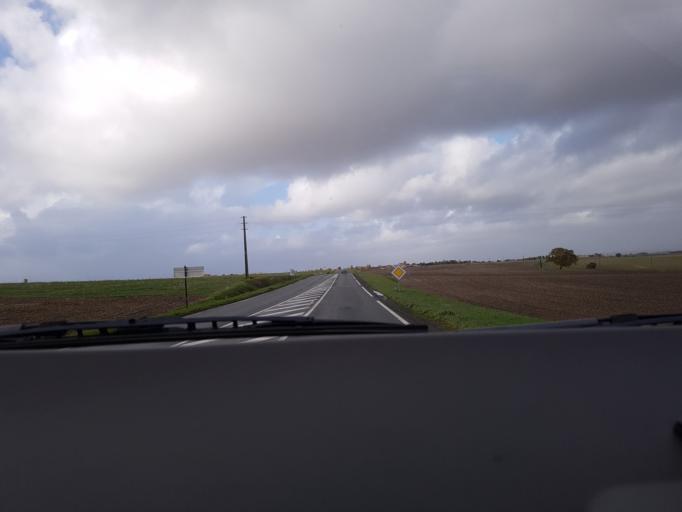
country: FR
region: Poitou-Charentes
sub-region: Departement de la Charente-Maritime
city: Pons
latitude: 45.6416
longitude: -0.5805
